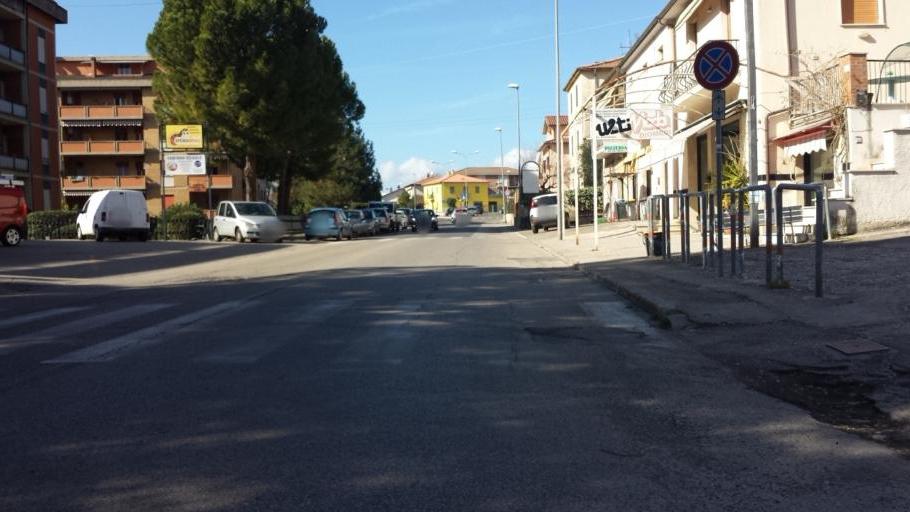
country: IT
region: Umbria
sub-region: Provincia di Terni
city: Terni
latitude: 42.5872
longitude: 12.6084
